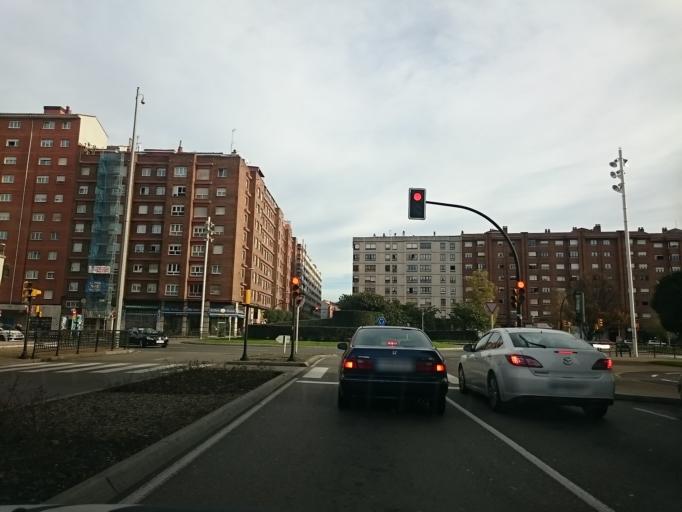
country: ES
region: Asturias
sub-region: Province of Asturias
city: Gijon
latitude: 43.5399
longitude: -5.6678
